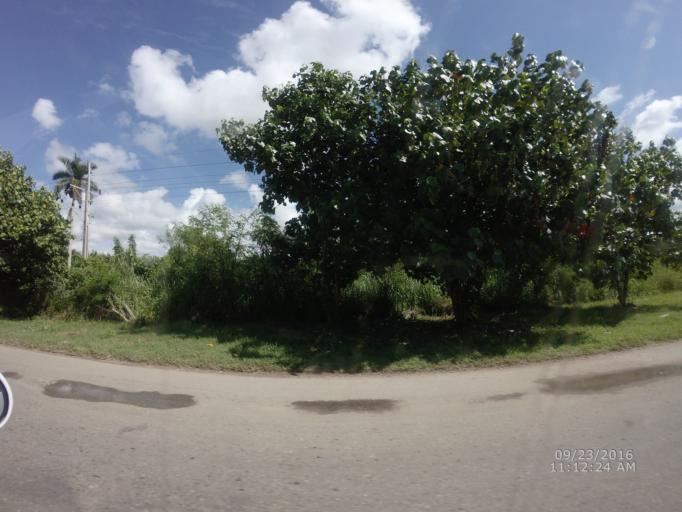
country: CU
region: La Habana
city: Arroyo Naranjo
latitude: 23.0293
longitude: -82.2832
